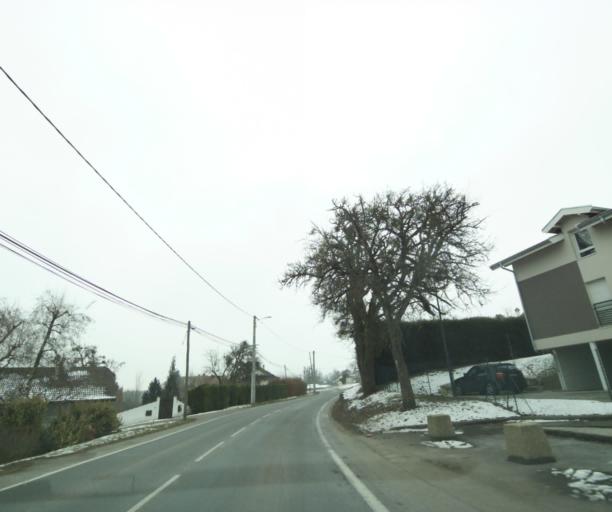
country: FR
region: Rhone-Alpes
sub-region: Departement de la Haute-Savoie
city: Reignier-Esery
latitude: 46.1278
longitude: 6.2747
